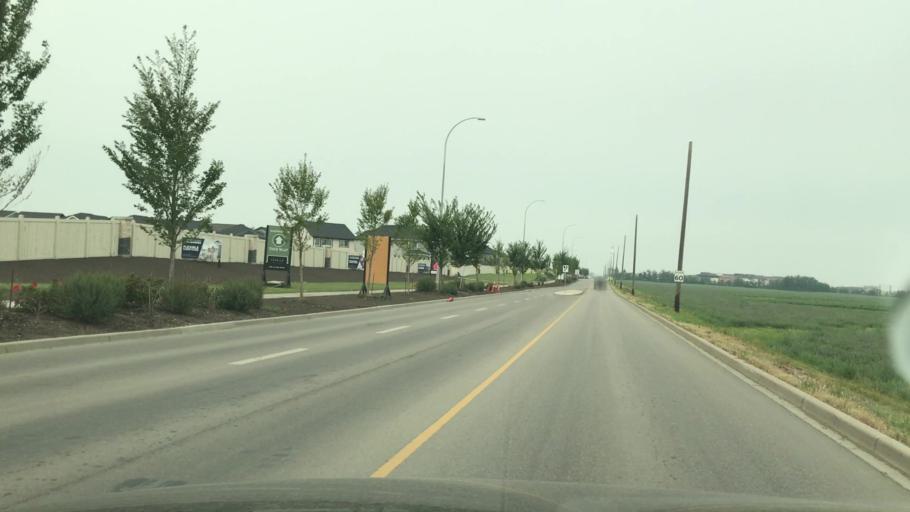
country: CA
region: Alberta
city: Devon
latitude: 53.4249
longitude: -113.5900
